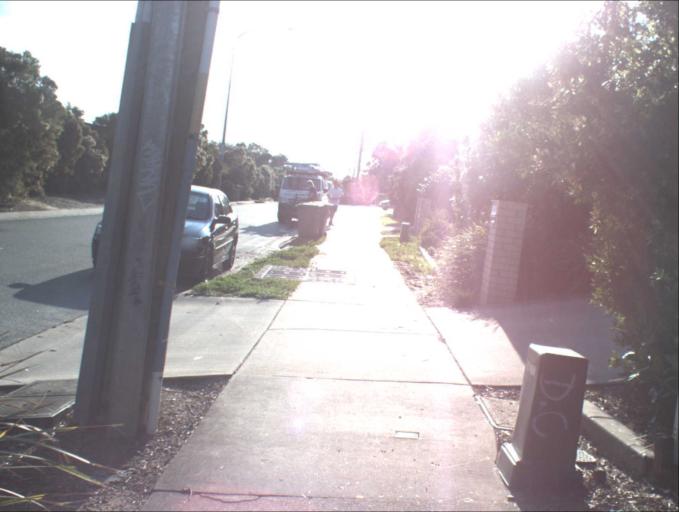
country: AU
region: Queensland
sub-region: Logan
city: Waterford West
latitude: -27.6948
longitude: 153.1529
